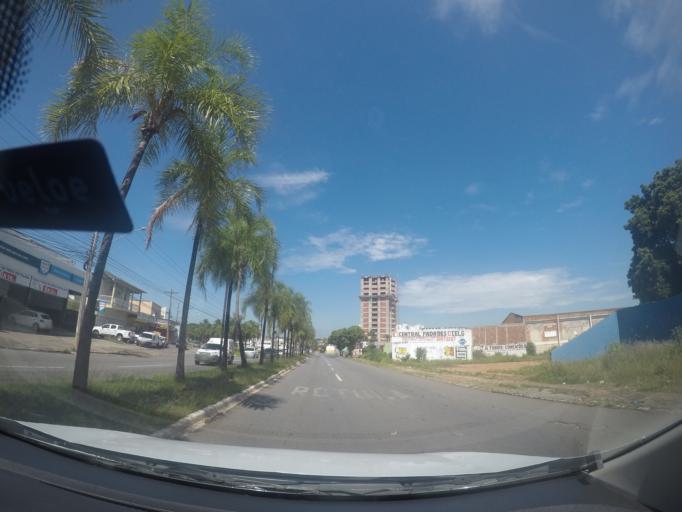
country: BR
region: Goias
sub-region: Goiania
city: Goiania
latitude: -16.7112
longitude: -49.3137
